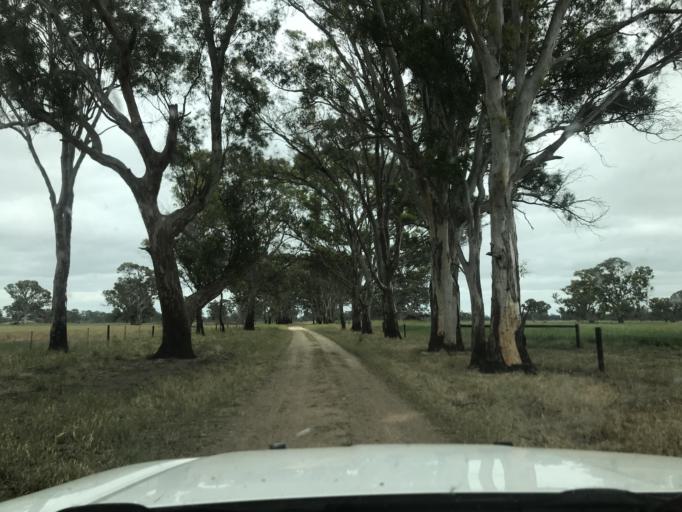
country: AU
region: South Australia
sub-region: Wattle Range
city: Penola
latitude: -37.1781
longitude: 141.0492
